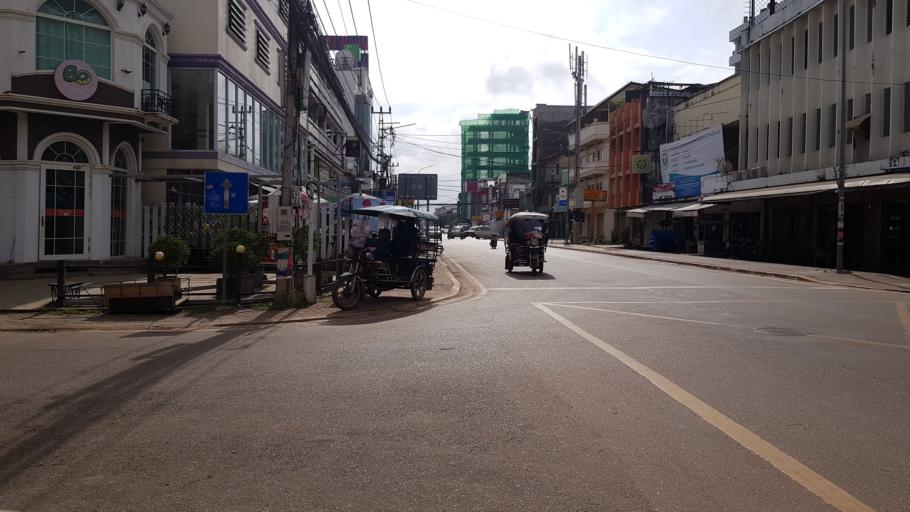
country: LA
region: Vientiane
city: Vientiane
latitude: 17.9684
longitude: 102.6041
